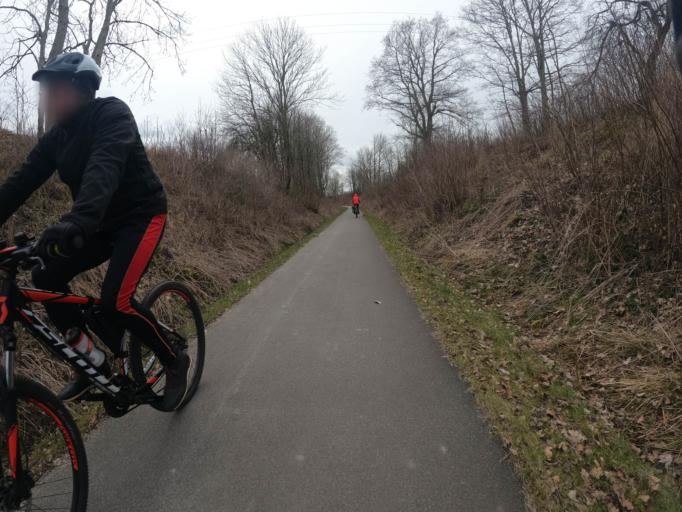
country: PL
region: West Pomeranian Voivodeship
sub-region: Powiat gryficki
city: Trzebiatow
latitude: 54.0823
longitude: 15.2615
